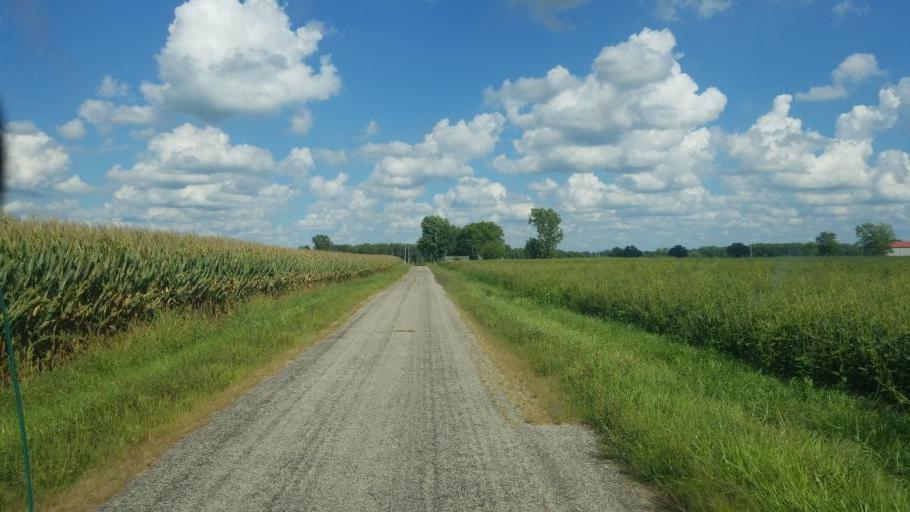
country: US
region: Ohio
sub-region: Union County
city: Richwood
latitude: 40.4661
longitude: -83.3306
